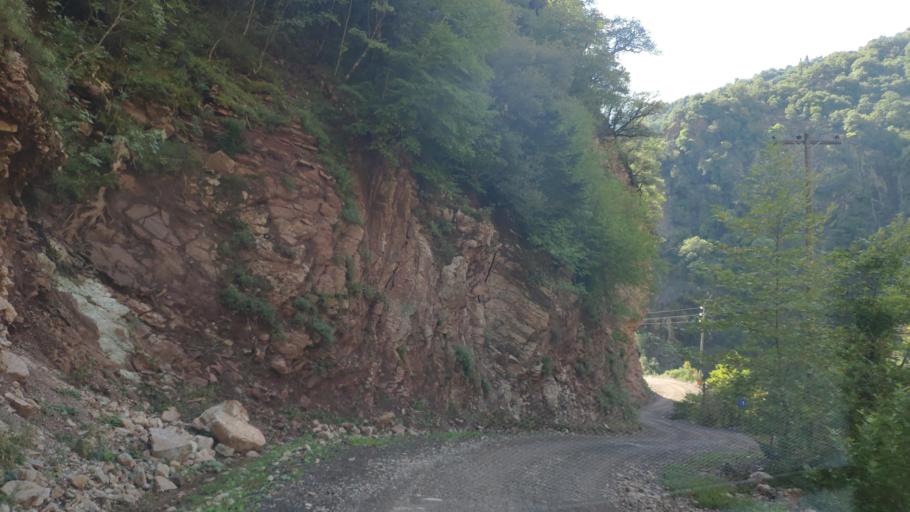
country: GR
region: Central Greece
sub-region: Nomos Evrytanias
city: Kerasochori
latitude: 39.1343
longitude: 21.6352
